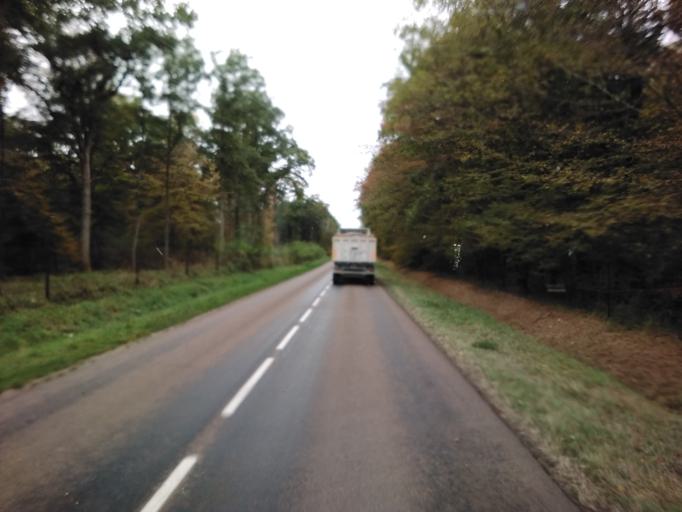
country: FR
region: Champagne-Ardenne
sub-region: Departement de l'Aube
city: Vendeuvre-sur-Barse
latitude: 48.2618
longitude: 4.4957
